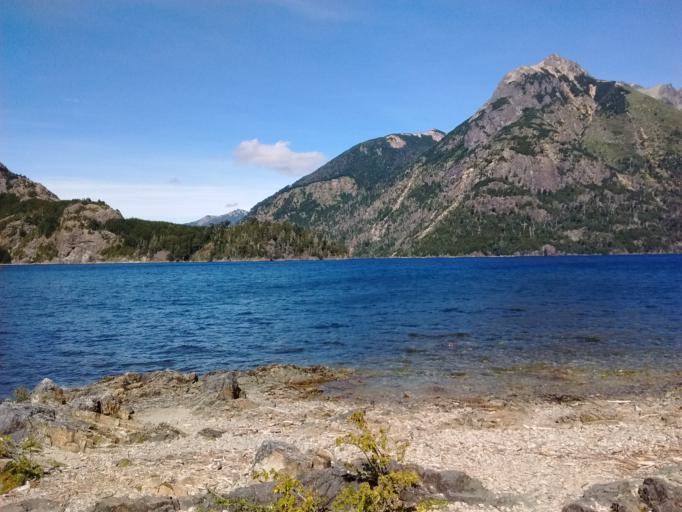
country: AR
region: Rio Negro
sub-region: Departamento de Bariloche
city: San Carlos de Bariloche
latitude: -41.0635
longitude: -71.5701
